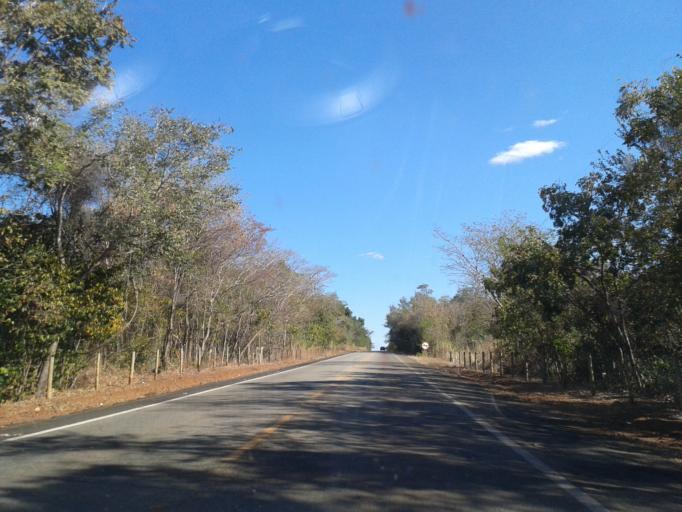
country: BR
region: Goias
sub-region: Mozarlandia
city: Mozarlandia
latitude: -14.6745
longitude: -50.5360
